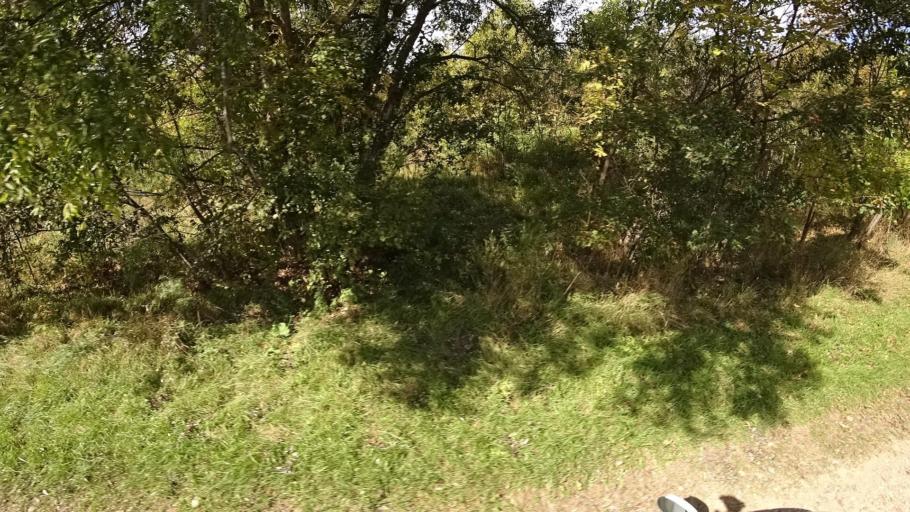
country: RU
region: Primorskiy
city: Kirovskiy
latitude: 44.7560
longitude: 133.6113
